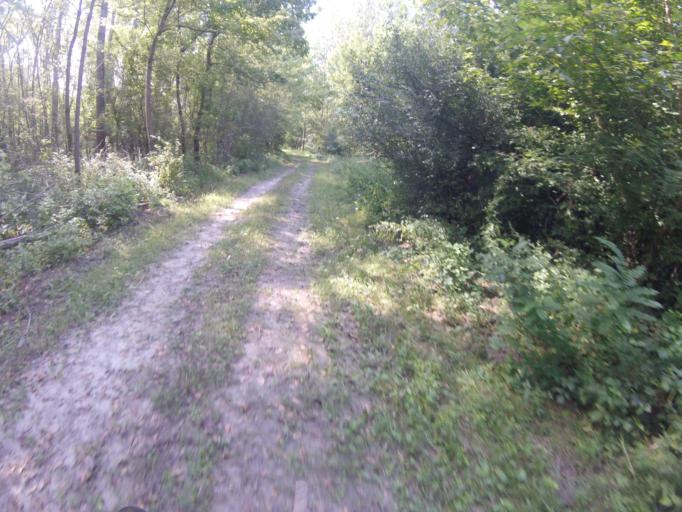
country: HU
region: Bacs-Kiskun
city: Baja
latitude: 46.2174
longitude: 18.8890
